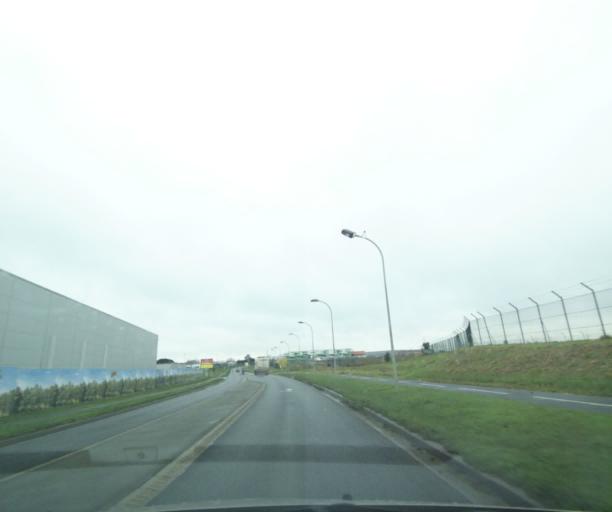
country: FR
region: Ile-de-France
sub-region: Departement du Val-de-Marne
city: Villeneuve-le-Roi
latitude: 48.7296
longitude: 2.4058
